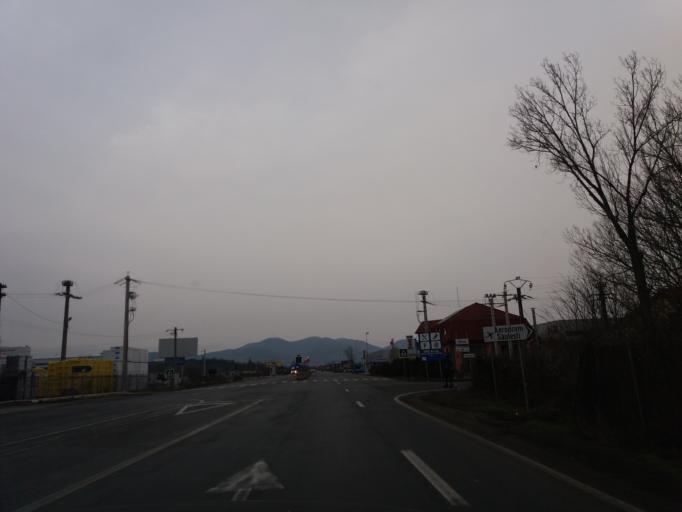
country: RO
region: Hunedoara
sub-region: Municipiul Deva
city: Cristur
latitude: 45.8535
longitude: 22.9655
